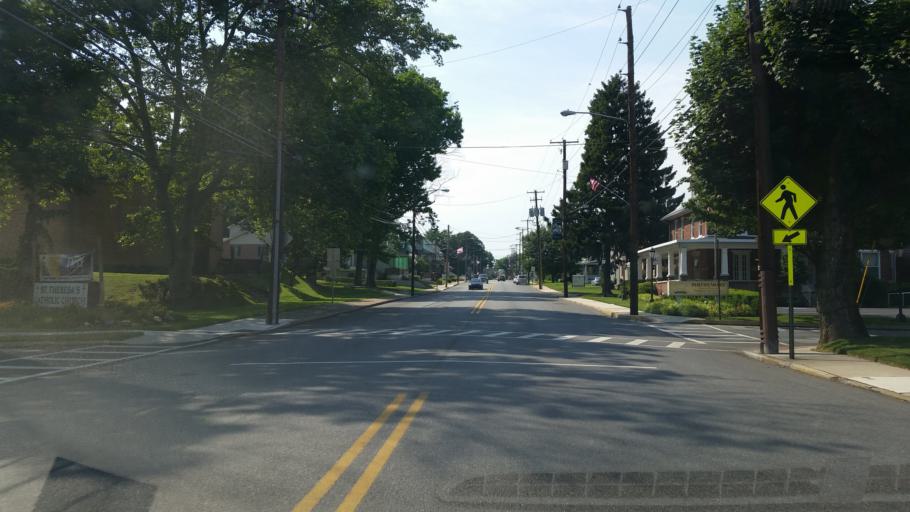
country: US
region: Pennsylvania
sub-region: Cumberland County
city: New Cumberland
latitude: 40.2337
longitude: -76.8750
